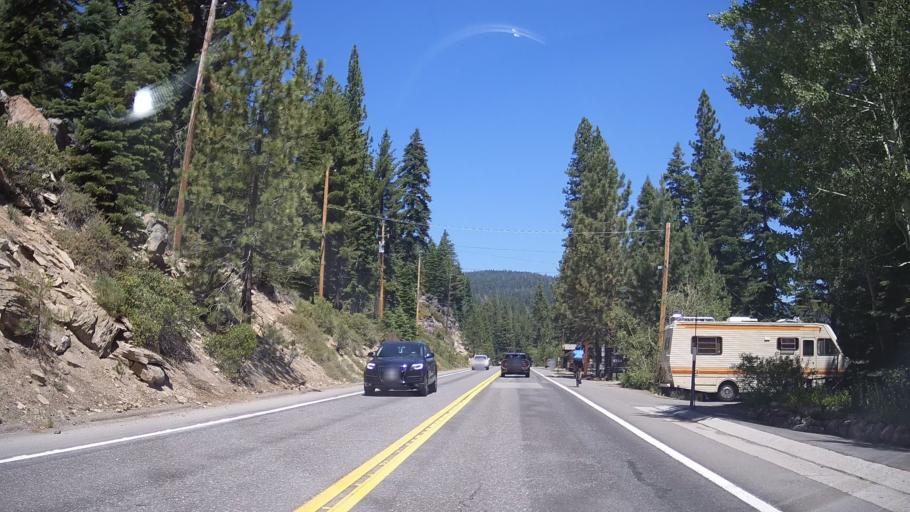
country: US
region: California
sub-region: Placer County
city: Dollar Point
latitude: 39.2201
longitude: -120.0869
